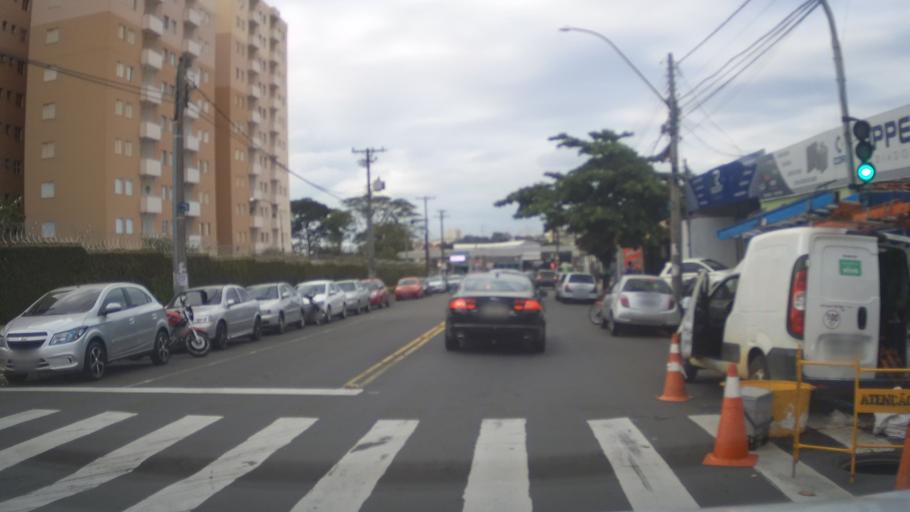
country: BR
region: Sao Paulo
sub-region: Campinas
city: Campinas
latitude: -22.9310
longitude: -47.0842
